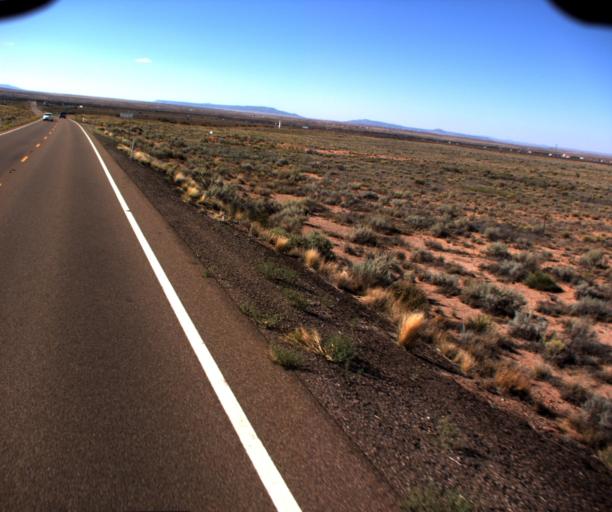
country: US
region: Arizona
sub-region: Navajo County
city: Winslow
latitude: 35.0205
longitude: -110.6332
